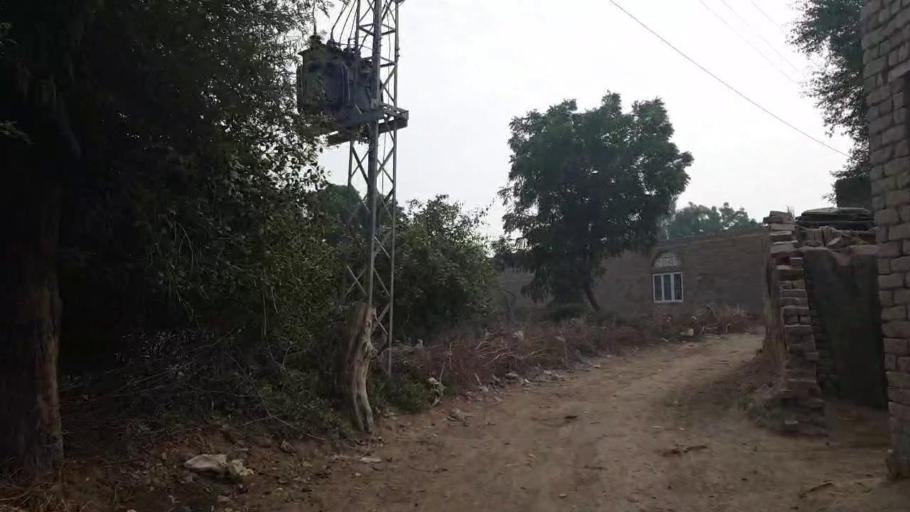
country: PK
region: Sindh
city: Sann
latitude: 25.9870
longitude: 68.1862
